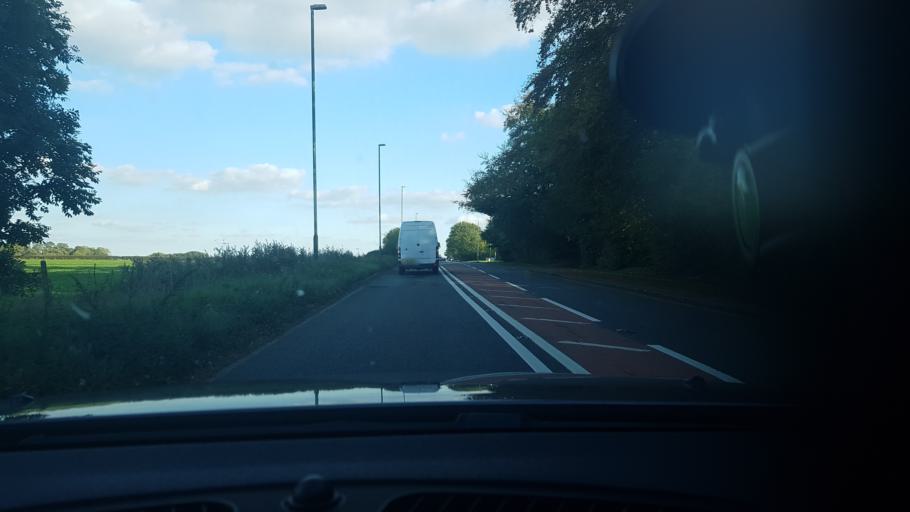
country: GB
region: England
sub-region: Gloucestershire
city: Cirencester
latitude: 51.7016
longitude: -1.9404
